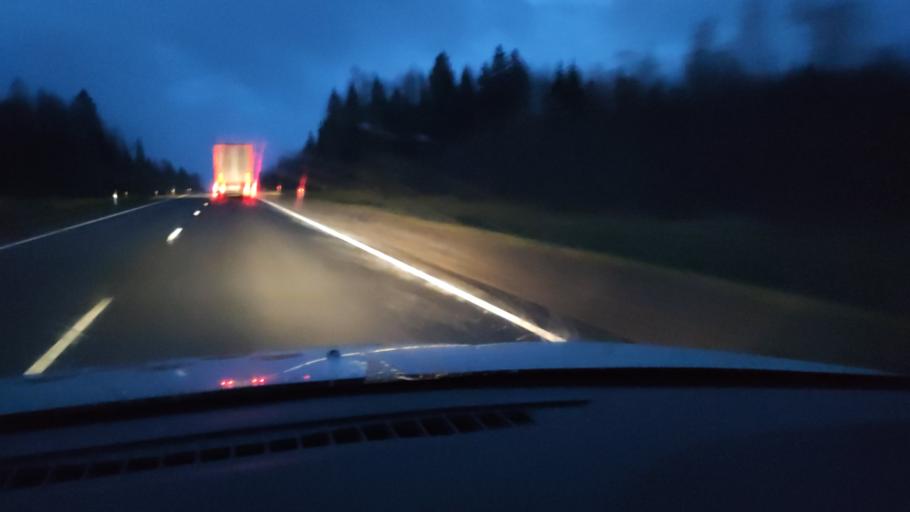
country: RU
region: Kirov
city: Kostino
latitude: 58.7684
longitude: 53.6097
